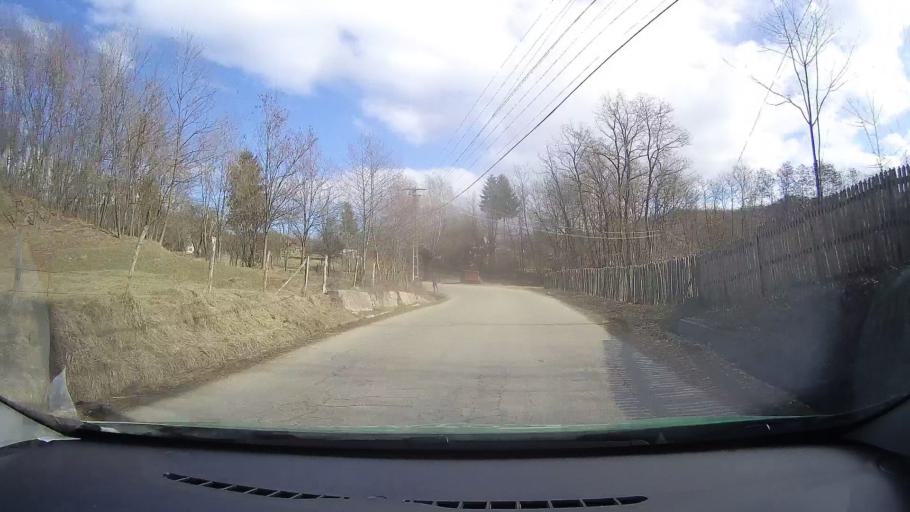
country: RO
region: Dambovita
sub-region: Comuna Varfuri
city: Varfuri
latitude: 45.0901
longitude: 25.5070
